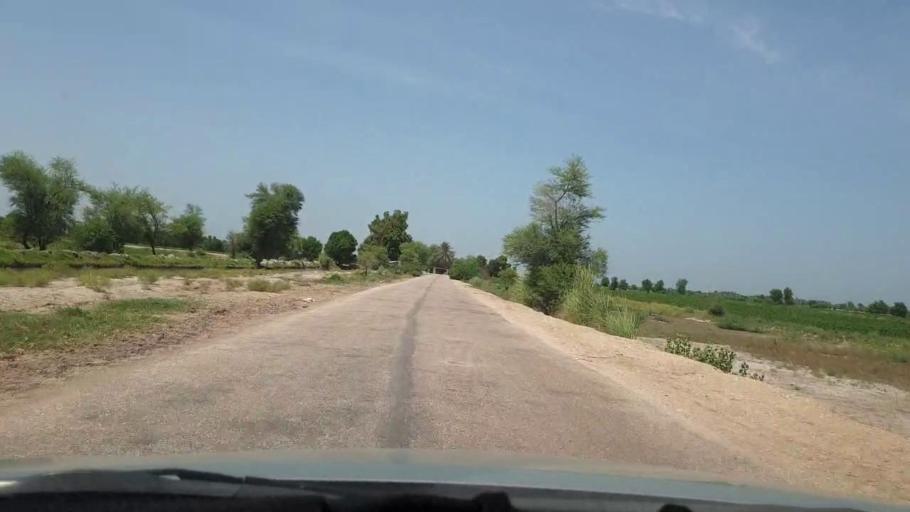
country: PK
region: Sindh
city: Pano Aqil
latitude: 27.6672
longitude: 69.1082
